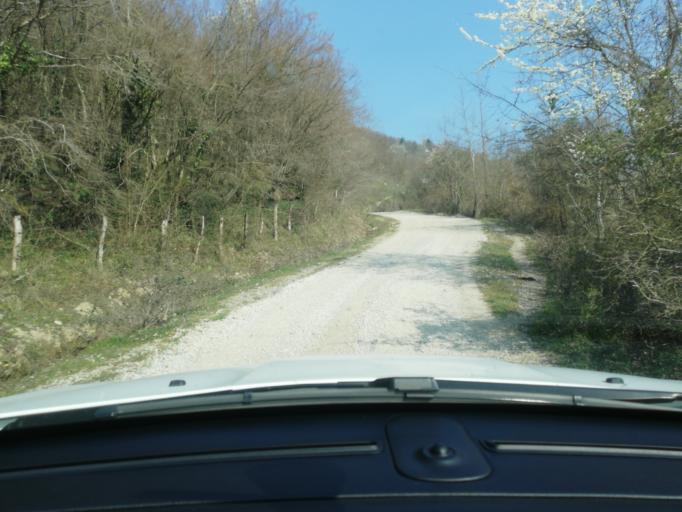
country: TR
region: Karabuk
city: Yenice
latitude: 41.2637
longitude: 32.3604
